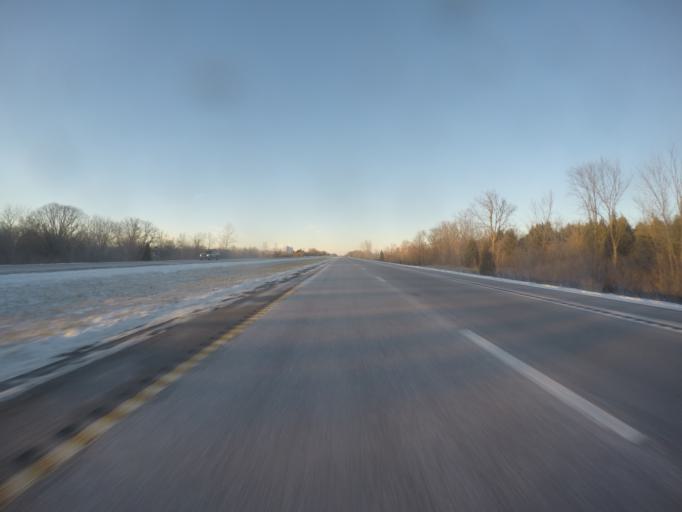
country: US
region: Missouri
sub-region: Platte County
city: Weatherby Lake
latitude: 39.2608
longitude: -94.7568
